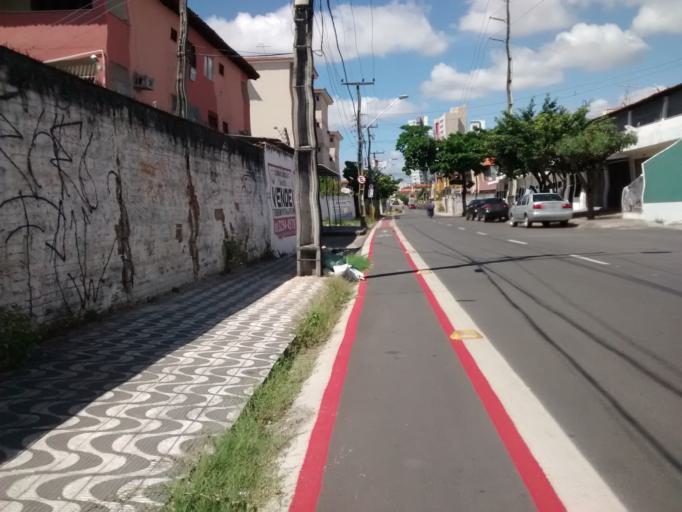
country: BR
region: Ceara
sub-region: Fortaleza
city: Fortaleza
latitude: -3.7304
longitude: -38.5601
